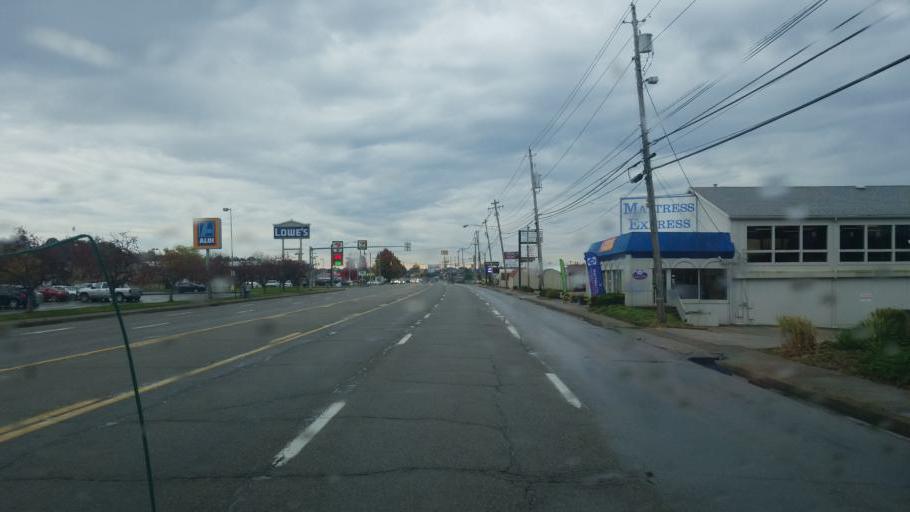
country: US
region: West Virginia
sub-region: Wood County
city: Vienna
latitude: 39.3138
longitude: -81.5535
